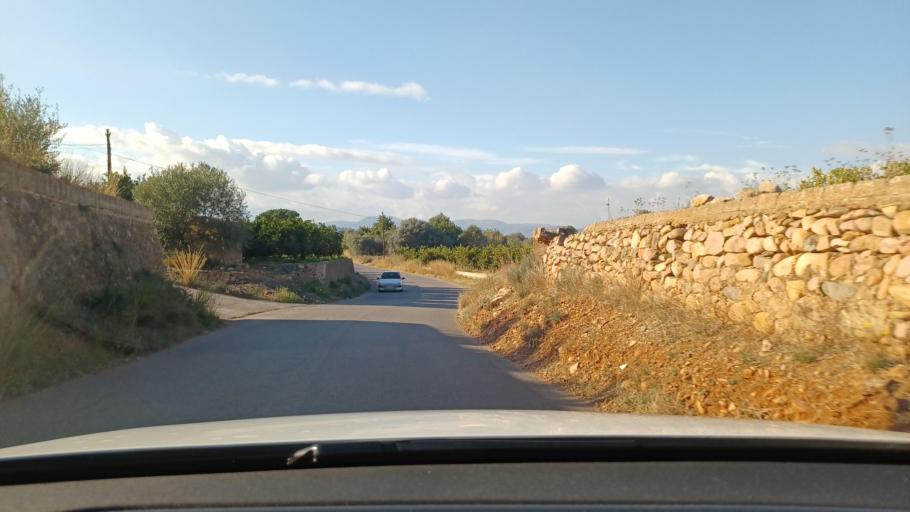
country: ES
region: Valencia
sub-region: Provincia de Castello
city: Betxi
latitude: 39.9460
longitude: -0.2196
